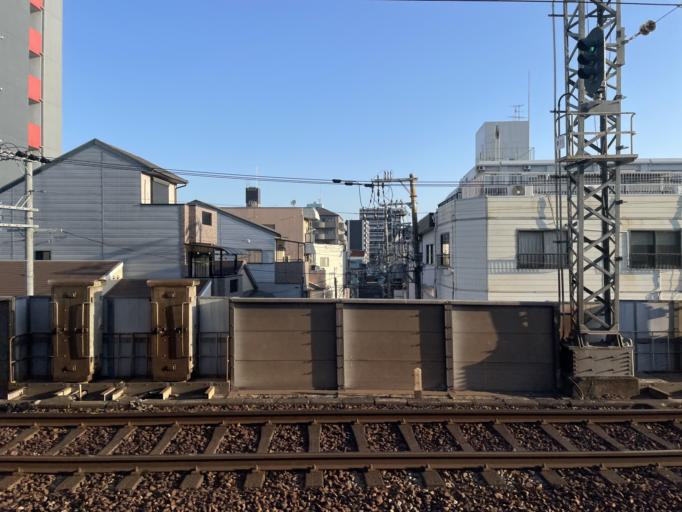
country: JP
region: Osaka
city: Osaka-shi
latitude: 34.6651
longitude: 135.5462
